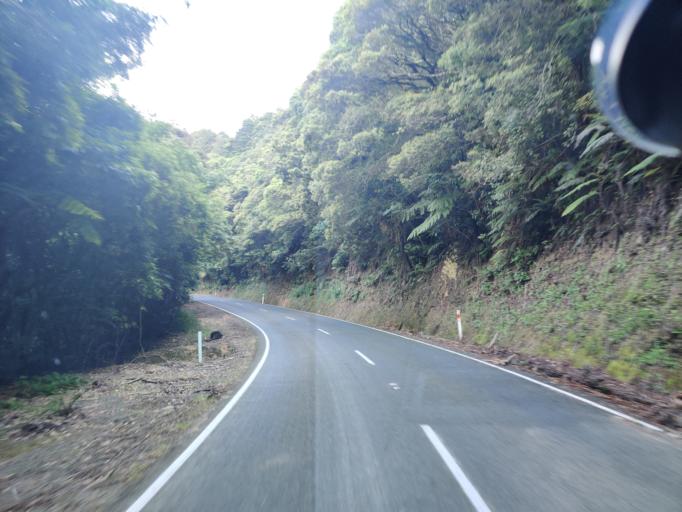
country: NZ
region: Northland
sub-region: Whangarei
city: Ngunguru
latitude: -35.5778
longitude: 174.4126
